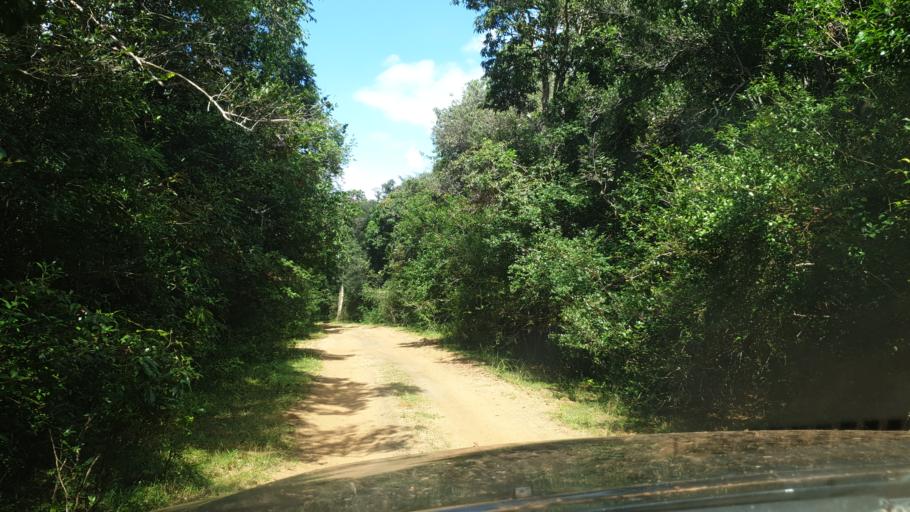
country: LK
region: North Central
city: Anuradhapura
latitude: 8.4229
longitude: 80.0111
